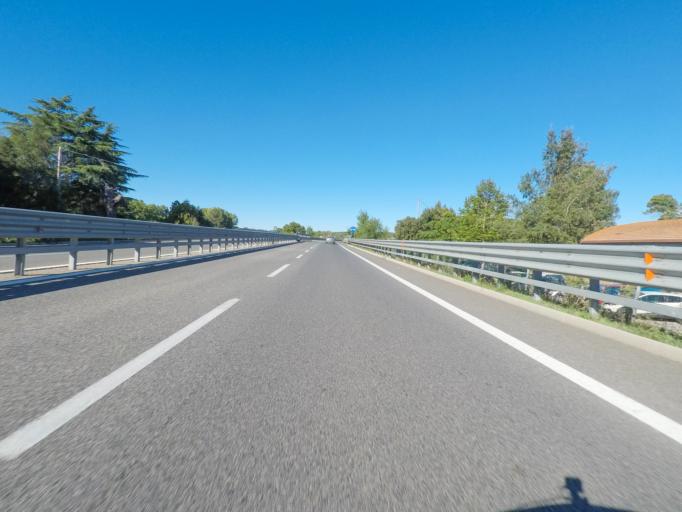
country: IT
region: Tuscany
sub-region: Provincia di Grosseto
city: Campagnatico
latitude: 42.9300
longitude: 11.2660
